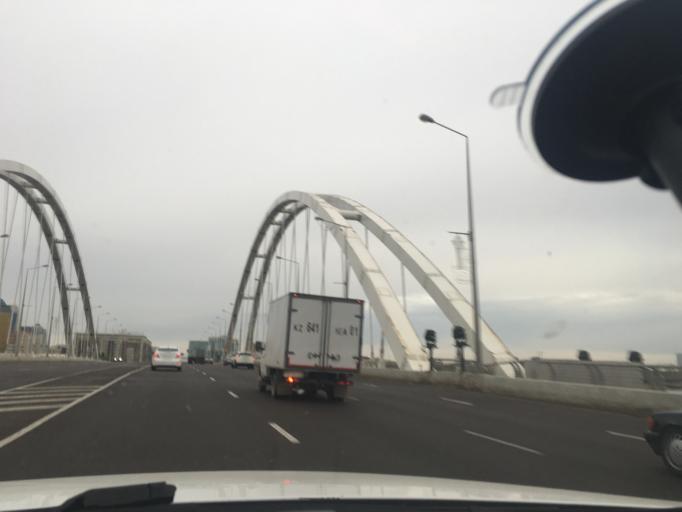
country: KZ
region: Astana Qalasy
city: Astana
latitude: 51.1310
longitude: 71.4489
